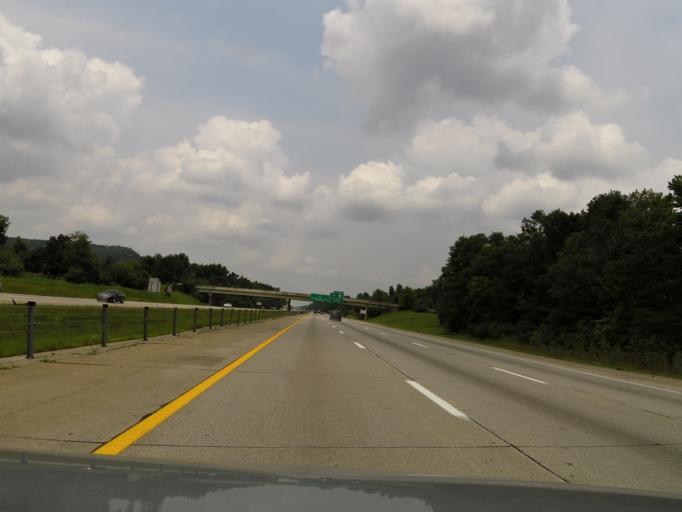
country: US
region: Kentucky
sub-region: Bullitt County
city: Hillview
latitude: 38.0896
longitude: -85.7010
